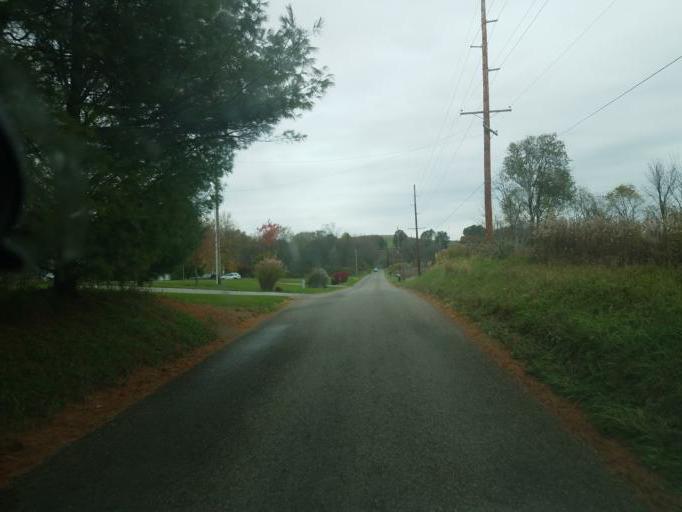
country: US
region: Ohio
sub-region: Ashland County
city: Loudonville
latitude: 40.6499
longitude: -82.2128
